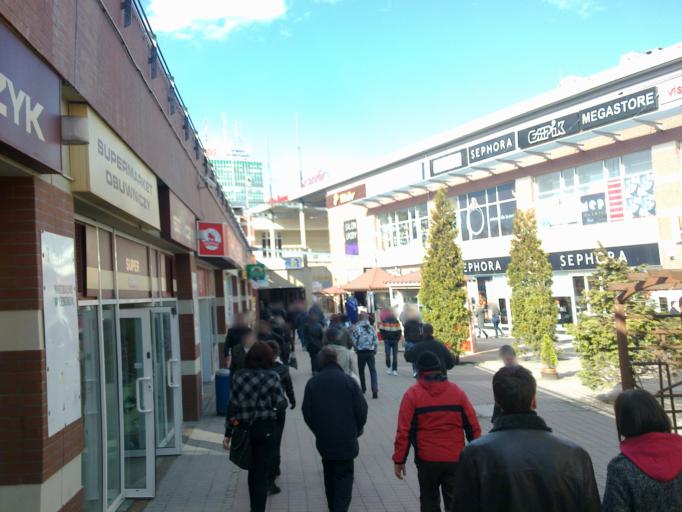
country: PL
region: Pomeranian Voivodeship
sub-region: Gdansk
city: Gdansk
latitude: 54.3554
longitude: 18.6463
